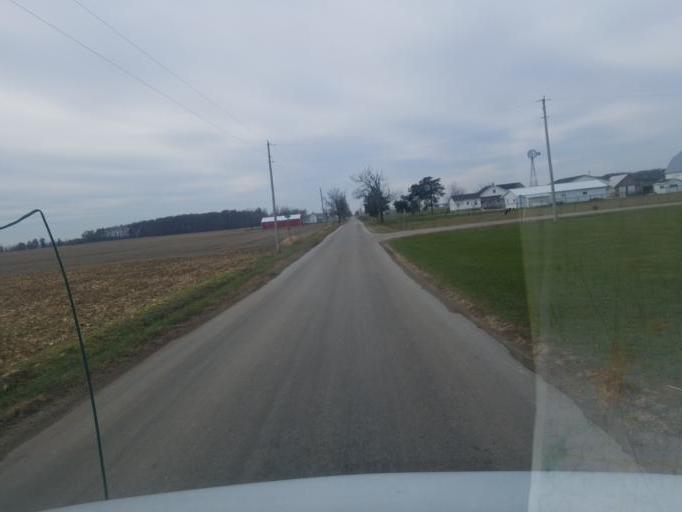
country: US
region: Indiana
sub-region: Adams County
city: Geneva
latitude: 40.6151
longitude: -84.8777
